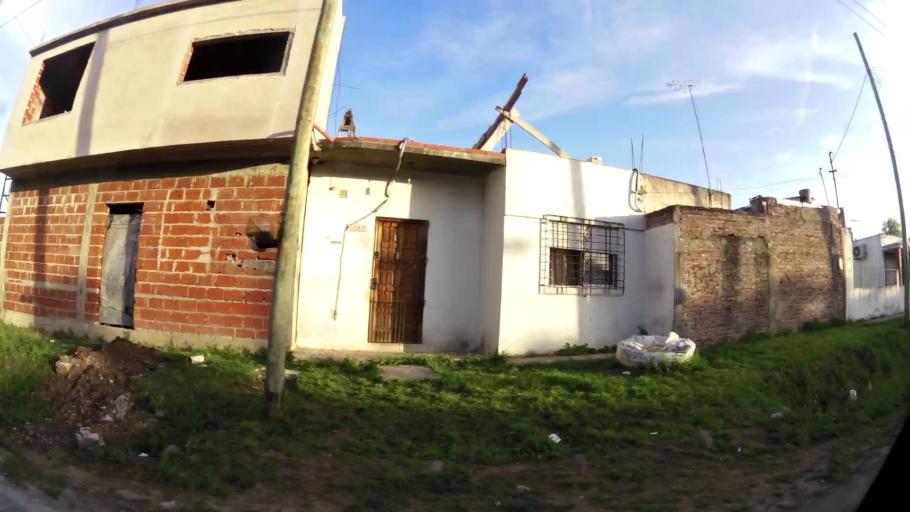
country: AR
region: Buenos Aires
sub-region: Partido de Quilmes
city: Quilmes
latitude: -34.7756
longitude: -58.2001
